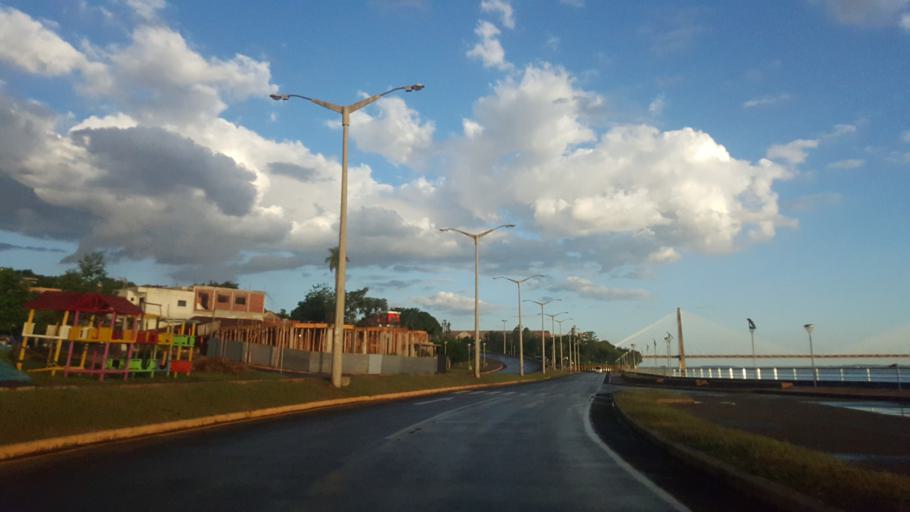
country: PY
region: Itapua
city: Encarnacion
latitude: -27.3601
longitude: -55.8636
